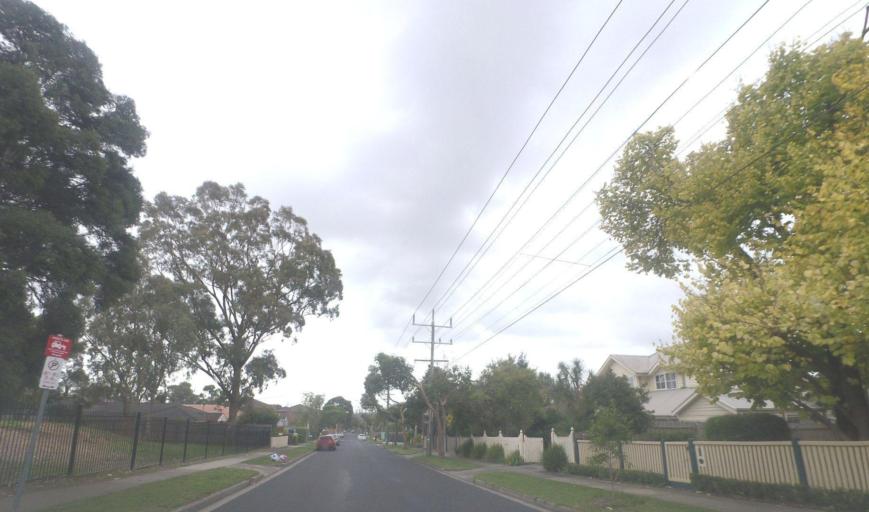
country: AU
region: Victoria
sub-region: Whitehorse
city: Blackburn North
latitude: -37.8068
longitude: 145.1528
